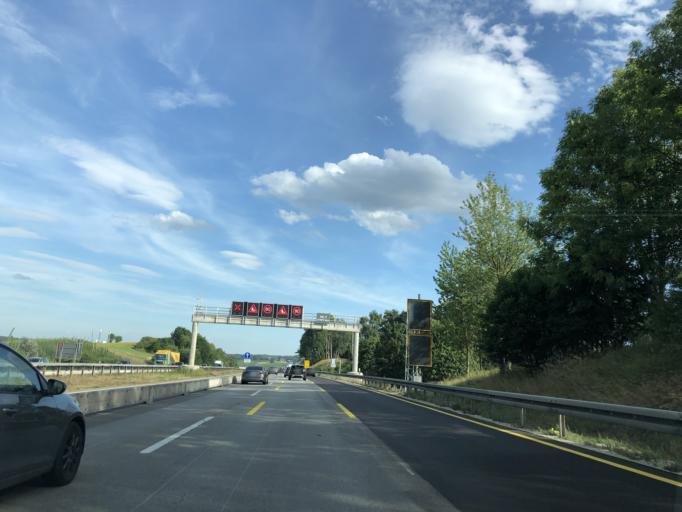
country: DE
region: Bavaria
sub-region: Upper Bavaria
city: Rohrbach
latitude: 48.6062
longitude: 11.5475
